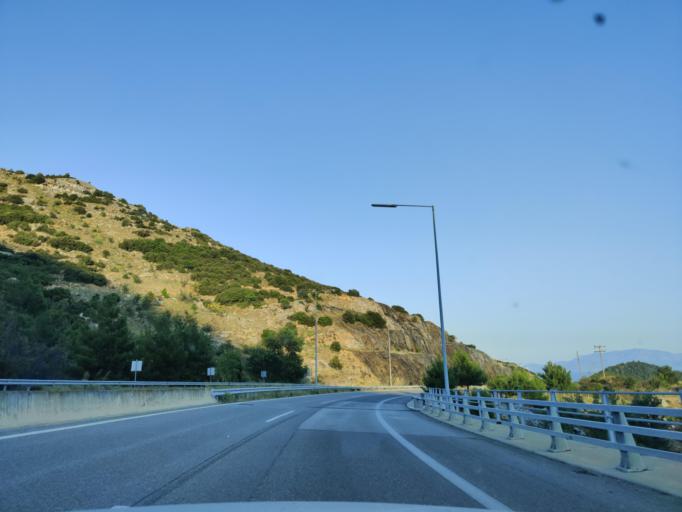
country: GR
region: East Macedonia and Thrace
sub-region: Nomos Kavalas
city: Kavala
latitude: 40.9651
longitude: 24.4321
